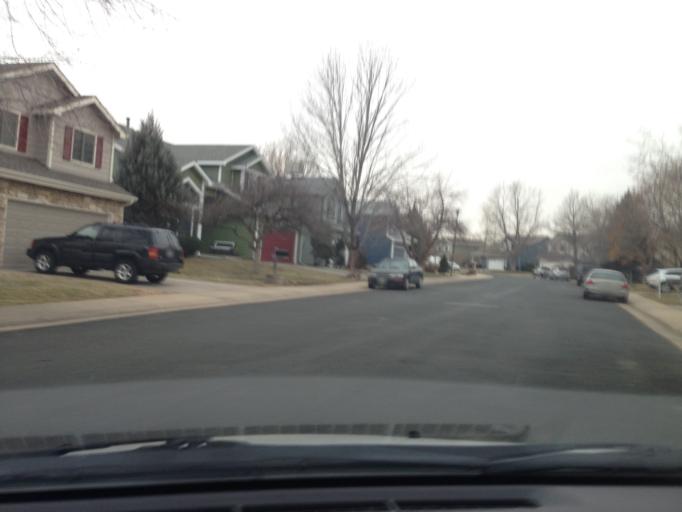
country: US
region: Colorado
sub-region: Boulder County
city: Superior
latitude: 39.9679
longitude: -105.1599
